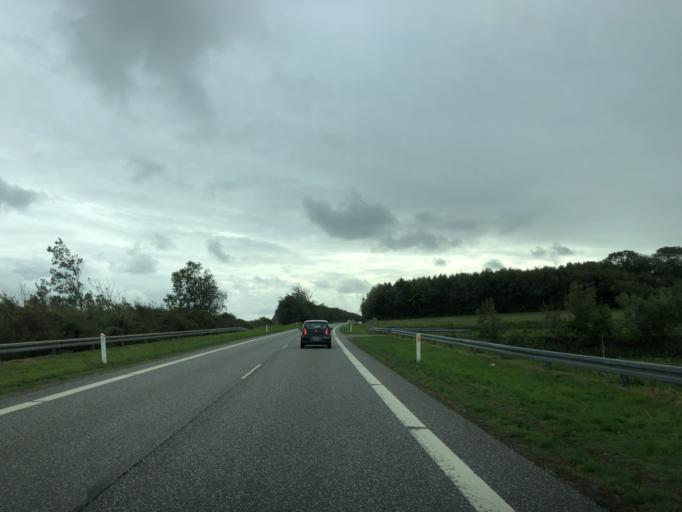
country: DK
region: North Denmark
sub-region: Thisted Kommune
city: Hurup
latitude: 56.7791
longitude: 8.4660
